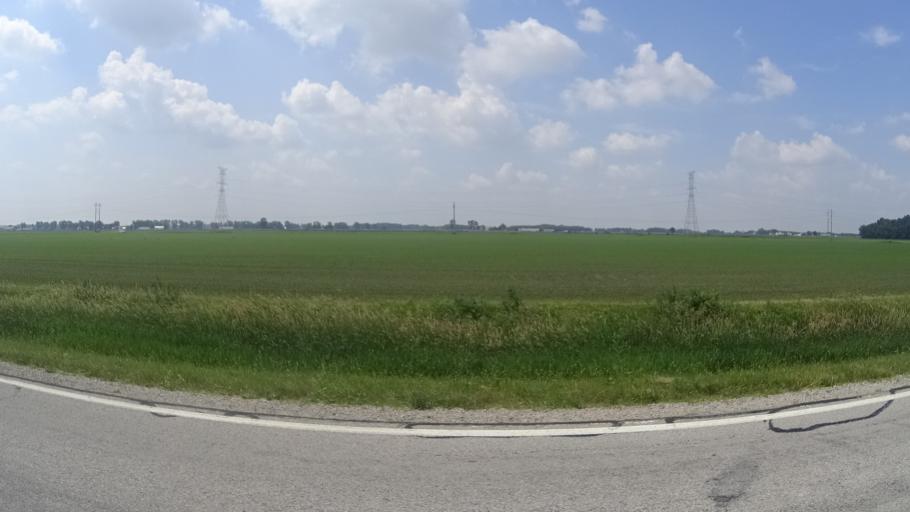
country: US
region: Ohio
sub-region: Erie County
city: Milan
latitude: 41.3369
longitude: -82.6552
